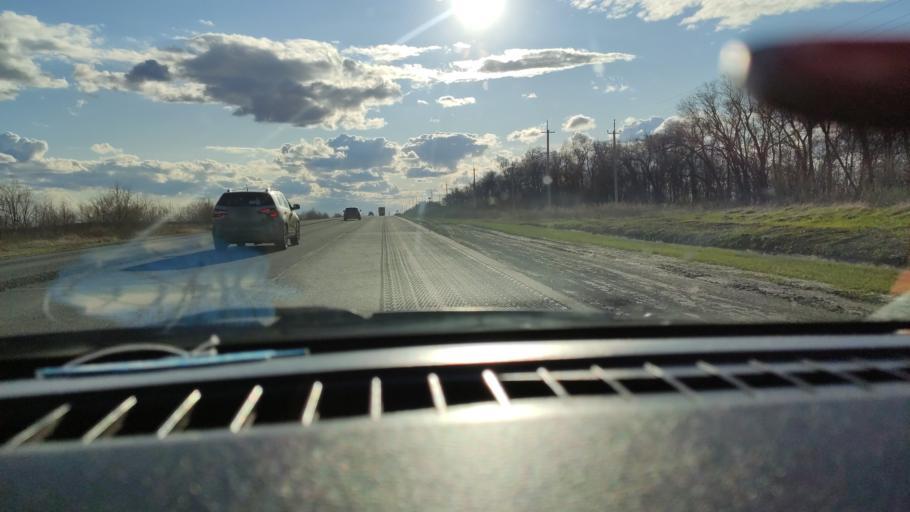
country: RU
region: Saratov
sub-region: Saratovskiy Rayon
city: Saratov
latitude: 51.7761
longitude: 46.1027
